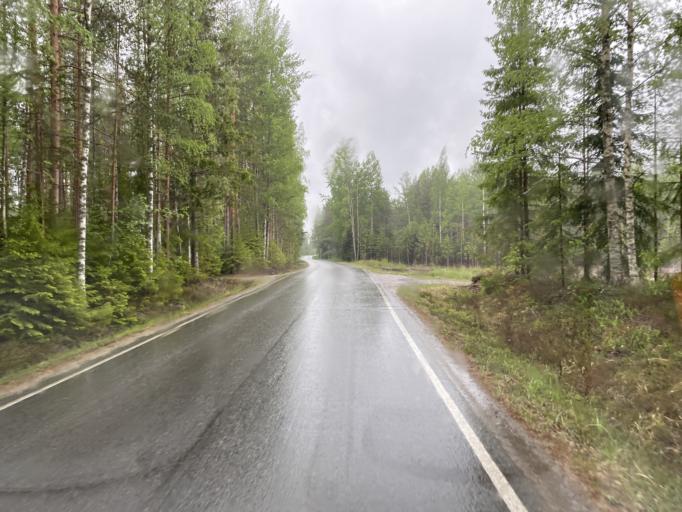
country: FI
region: Haeme
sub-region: Forssa
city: Humppila
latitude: 61.0859
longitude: 23.3097
